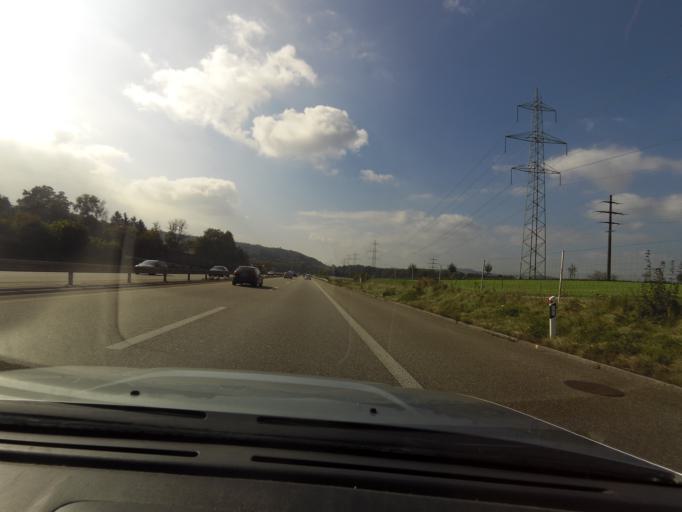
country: CH
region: Aargau
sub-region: Bezirk Rheinfelden
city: Mohlin
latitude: 47.5466
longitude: 7.8288
